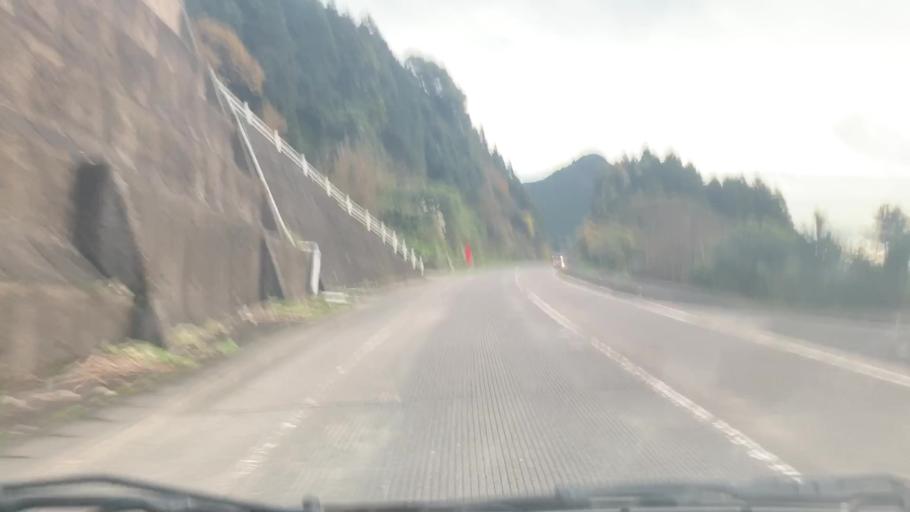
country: JP
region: Saga Prefecture
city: Kashima
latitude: 33.0556
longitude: 130.0716
